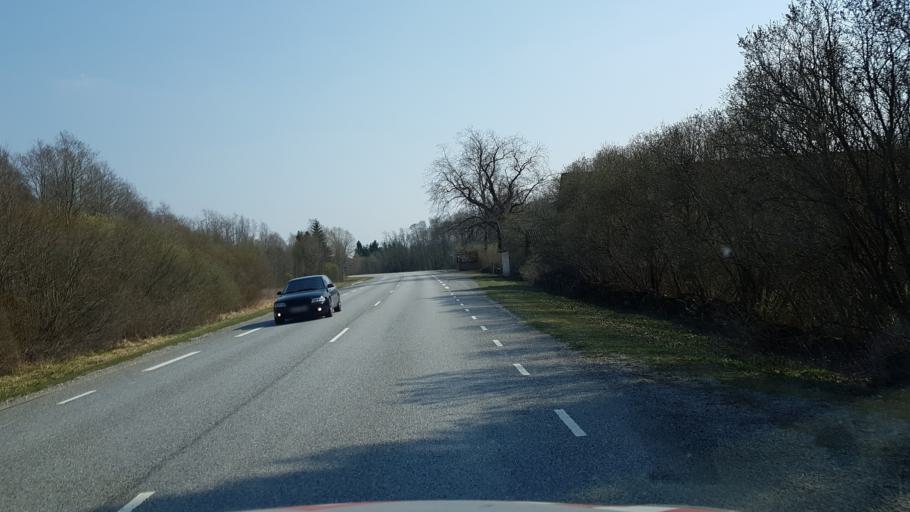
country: EE
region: Harju
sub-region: Paldiski linn
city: Paldiski
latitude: 59.2488
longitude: 23.9190
